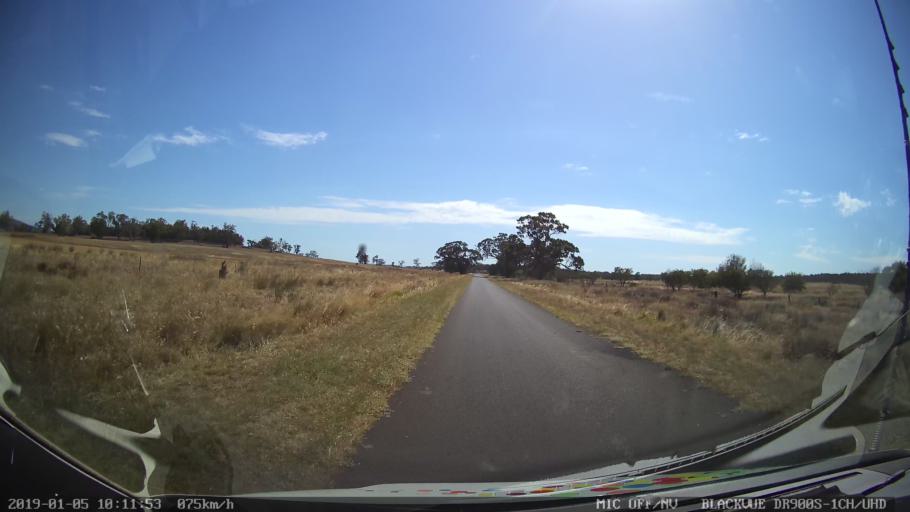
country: AU
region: New South Wales
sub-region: Gilgandra
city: Gilgandra
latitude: -31.6108
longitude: 148.9064
